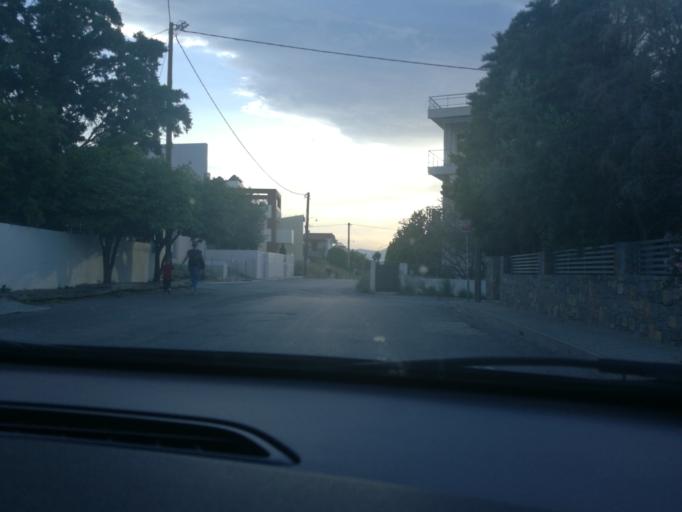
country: GR
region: Crete
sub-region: Nomos Irakleiou
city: Irakleion
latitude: 35.3187
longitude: 25.1474
